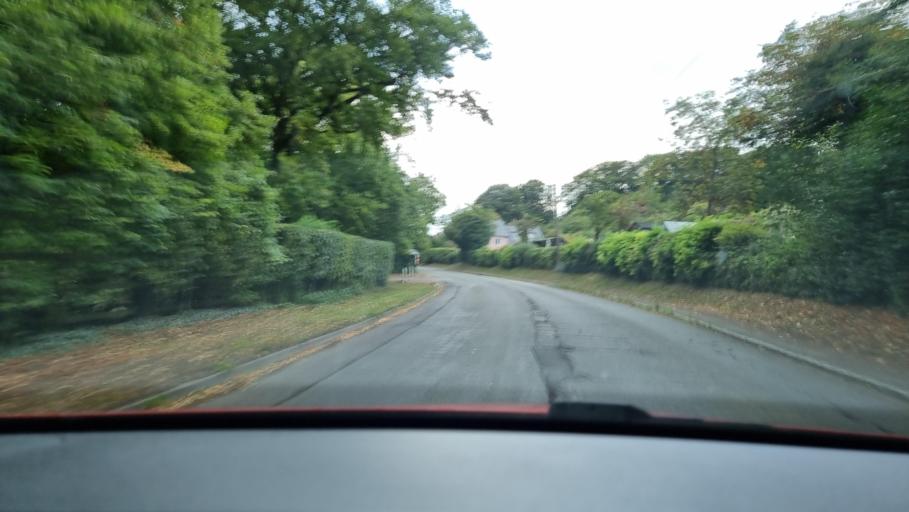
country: GB
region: England
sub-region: Buckinghamshire
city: Ivinghoe
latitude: 51.8356
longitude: -0.6267
